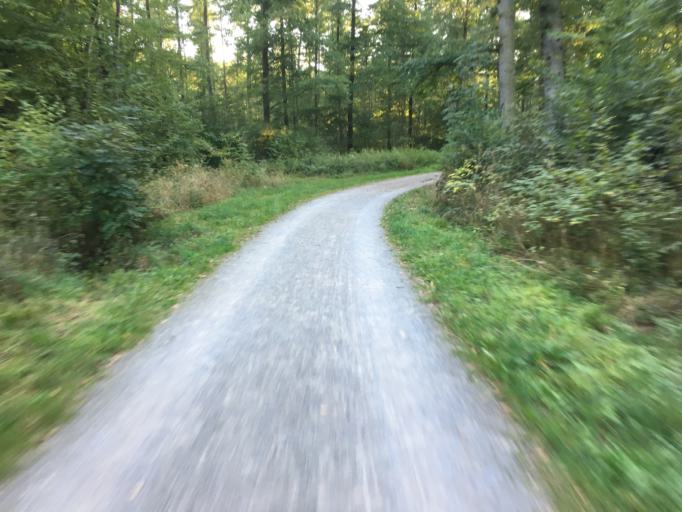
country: DE
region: Baden-Wuerttemberg
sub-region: Regierungsbezirk Stuttgart
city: Boeblingen
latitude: 48.6640
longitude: 8.9957
